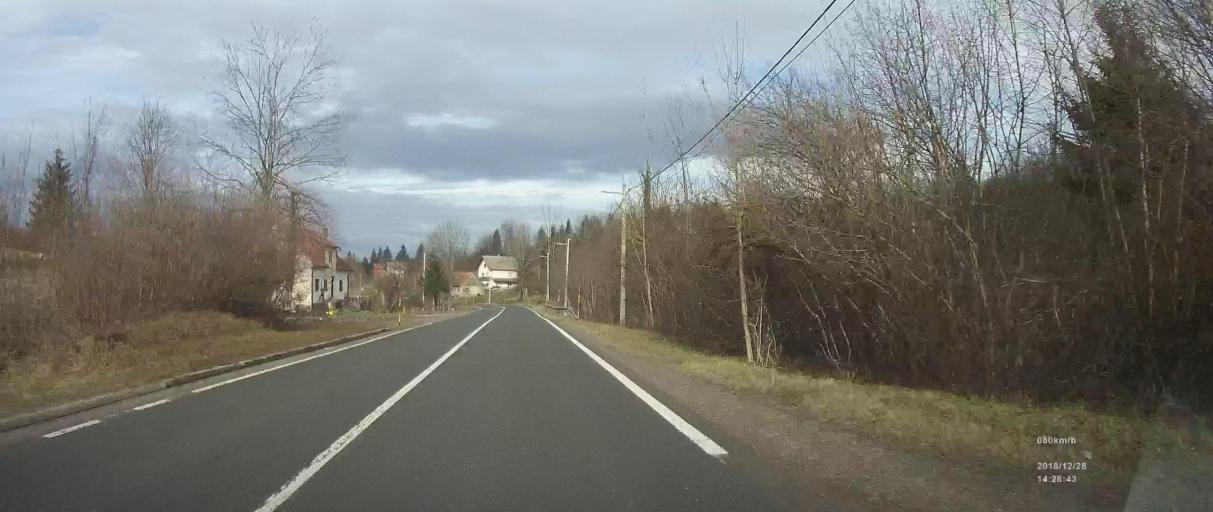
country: HR
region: Primorsko-Goranska
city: Vrbovsko
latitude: 45.4131
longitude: 15.1165
